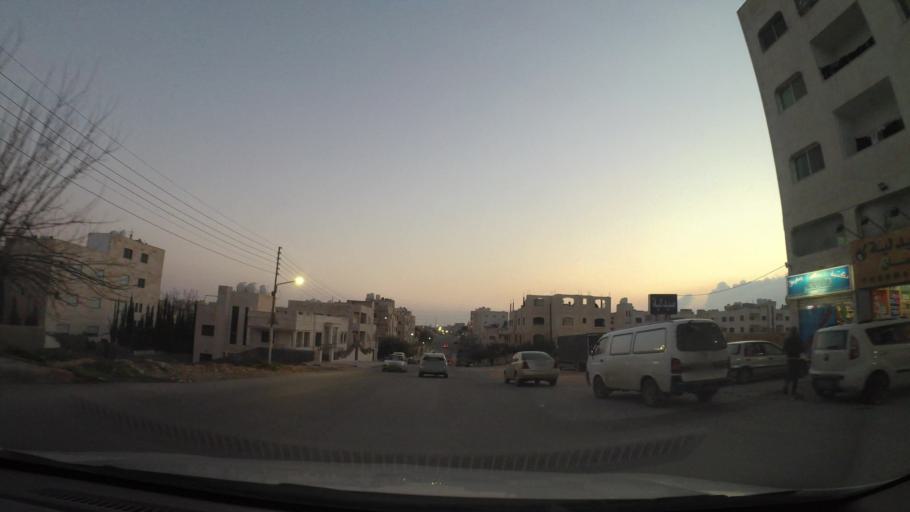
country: JO
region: Amman
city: Al Bunayyat ash Shamaliyah
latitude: 31.8890
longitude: 35.9247
